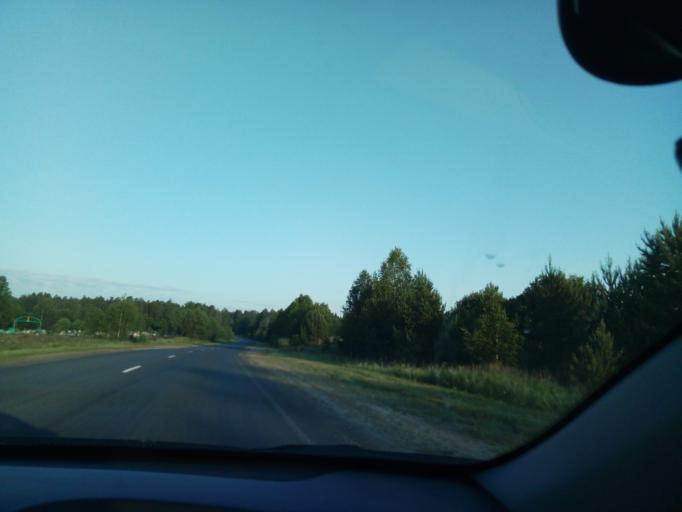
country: RU
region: Nizjnij Novgorod
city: Satis
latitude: 54.9352
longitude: 43.2294
